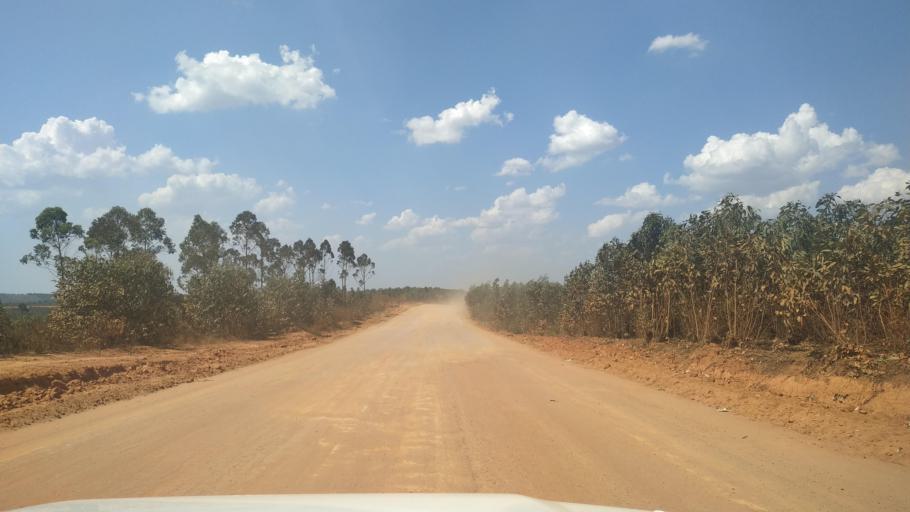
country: MG
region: Alaotra Mangoro
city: Ambatondrazaka
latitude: -18.1206
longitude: 48.2641
